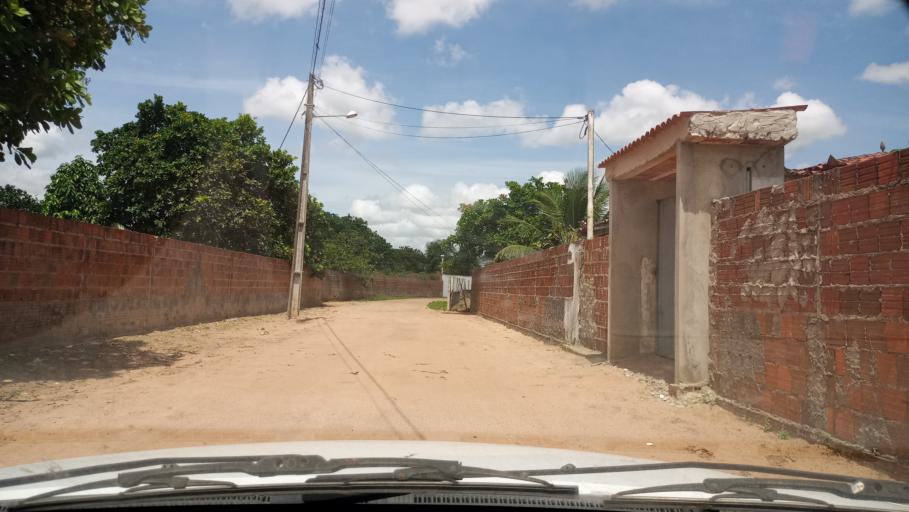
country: BR
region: Rio Grande do Norte
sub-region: Brejinho
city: Brejinho
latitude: -6.2629
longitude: -35.3705
